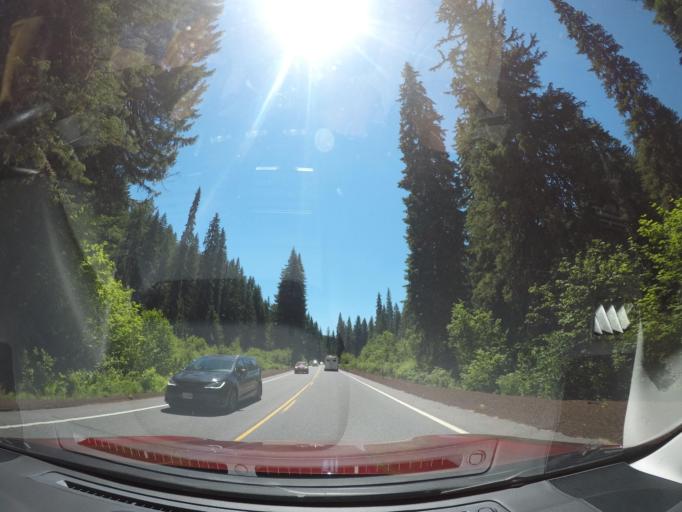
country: US
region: Oregon
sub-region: Deschutes County
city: Sisters
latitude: 44.5419
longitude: -121.9961
